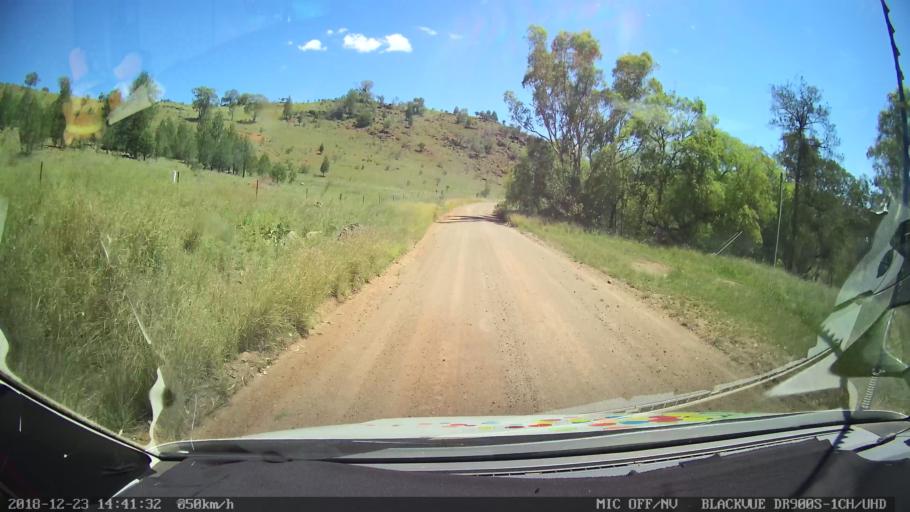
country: AU
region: New South Wales
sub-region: Tamworth Municipality
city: Manilla
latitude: -30.6321
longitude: 150.9017
